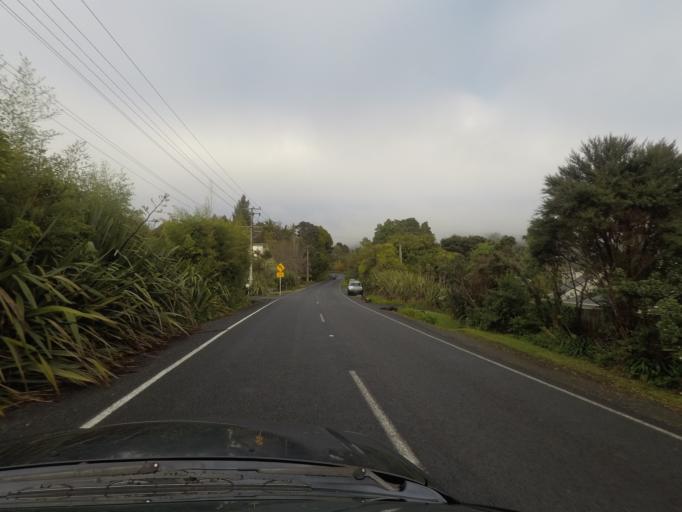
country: NZ
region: Auckland
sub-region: Auckland
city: Waitakere
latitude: -36.9202
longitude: 174.5855
